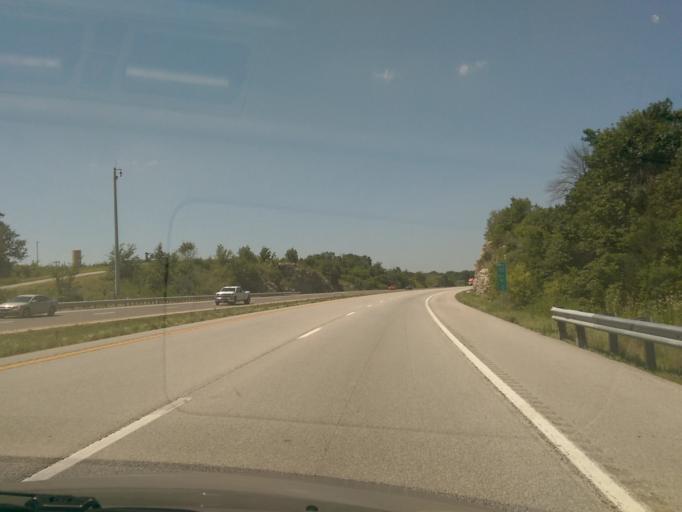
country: US
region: Missouri
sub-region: Cooper County
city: Boonville
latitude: 38.9346
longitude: -92.9773
